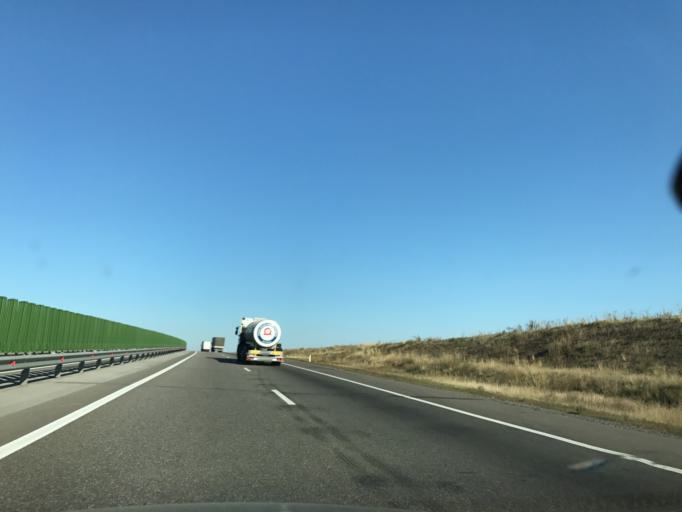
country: RU
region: Rostov
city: Tarasovskiy
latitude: 48.7369
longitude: 40.4005
